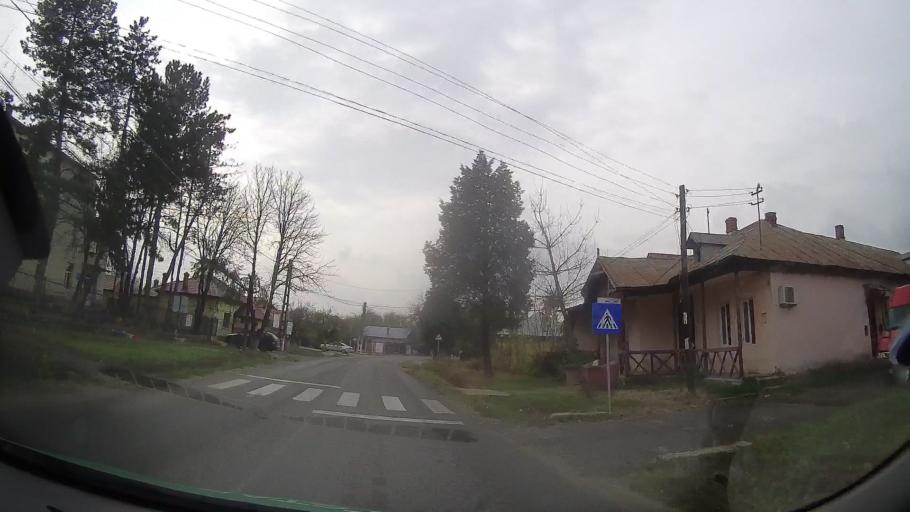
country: RO
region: Ilfov
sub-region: Comuna Gruiu
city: Gruiu
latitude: 44.7248
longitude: 26.2250
